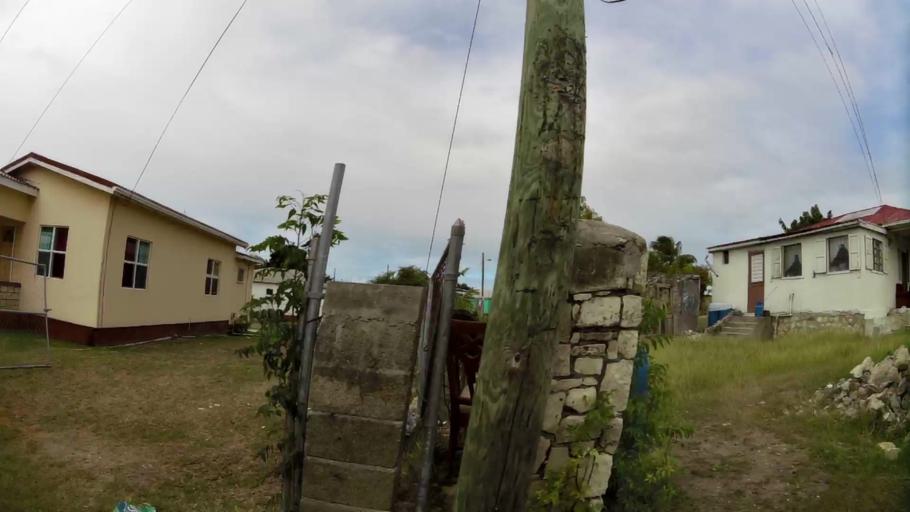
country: AG
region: Saint Peter
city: Parham
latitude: 17.0858
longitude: -61.7102
